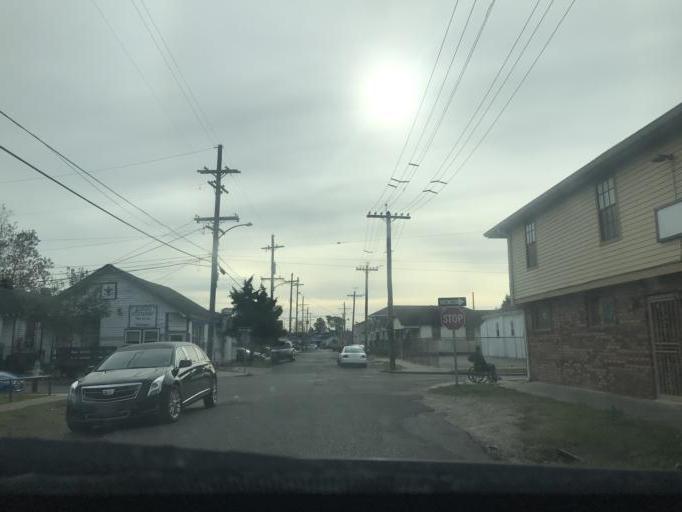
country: US
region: Louisiana
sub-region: Orleans Parish
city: New Orleans
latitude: 29.9578
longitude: -90.1111
